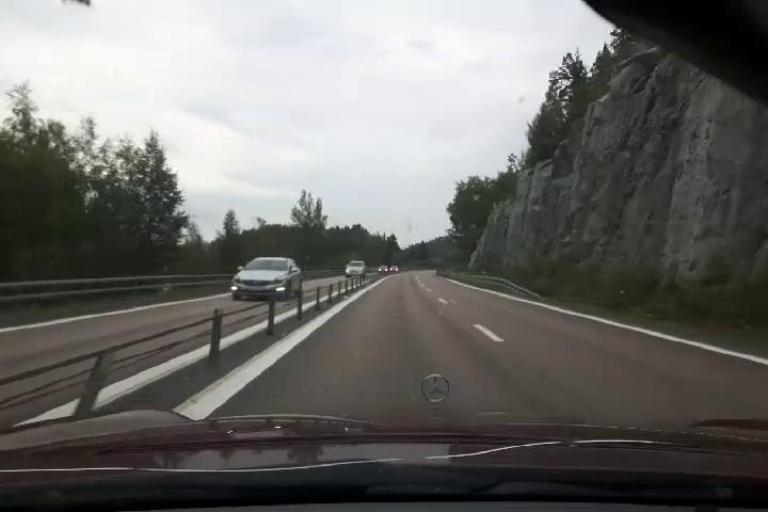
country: SE
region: Vaesternorrland
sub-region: Haernoesands Kommun
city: Haernoesand
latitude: 62.8191
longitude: 17.9695
